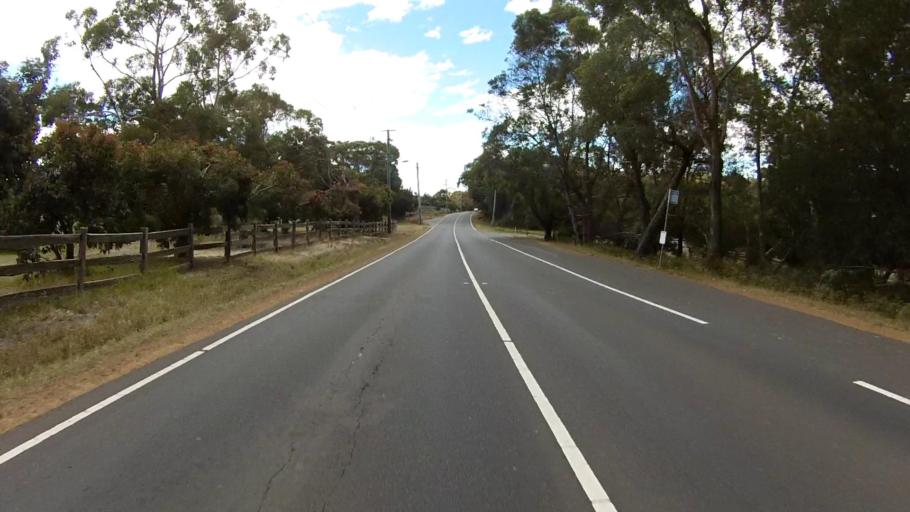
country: AU
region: Tasmania
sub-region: Clarence
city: Acton Park
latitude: -42.8794
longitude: 147.4819
